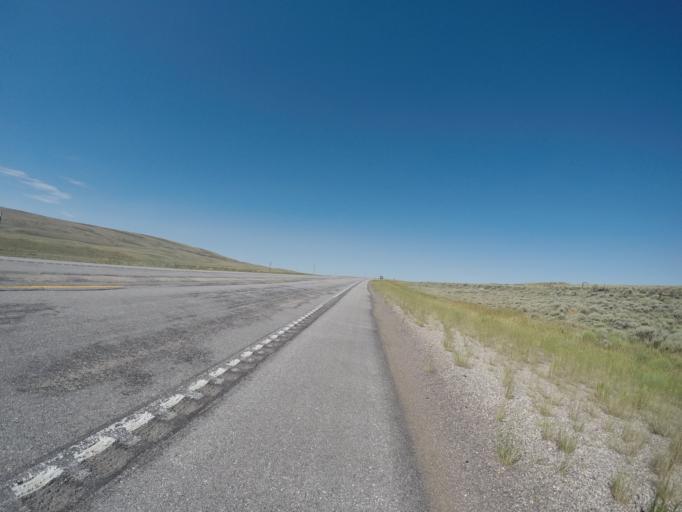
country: US
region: Wyoming
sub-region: Carbon County
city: Saratoga
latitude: 41.7966
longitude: -106.7211
